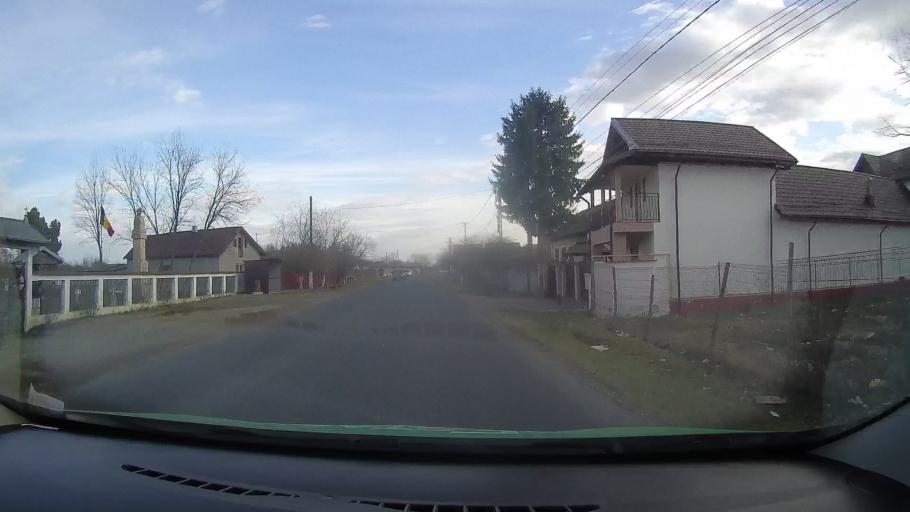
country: RO
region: Dambovita
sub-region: Municipiul Targoviste
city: Targoviste
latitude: 44.8926
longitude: 25.4599
